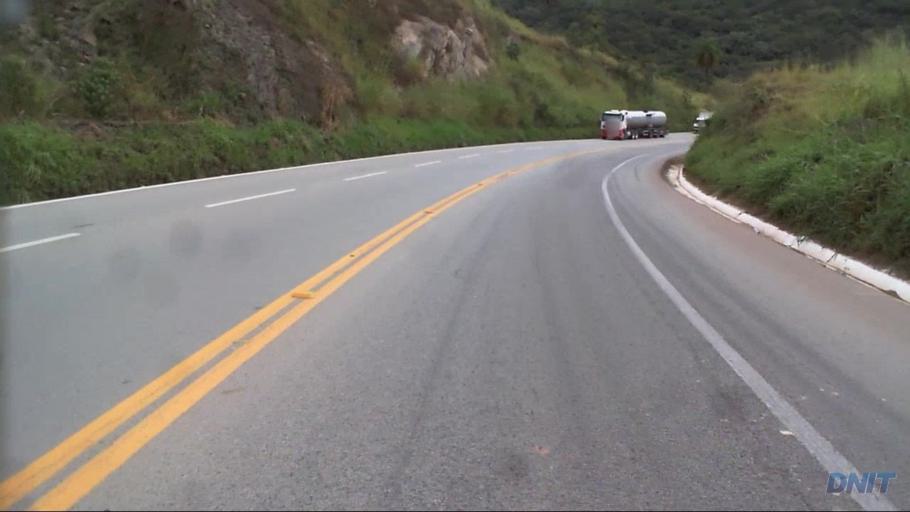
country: BR
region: Minas Gerais
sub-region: Caete
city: Caete
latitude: -19.7864
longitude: -43.6623
